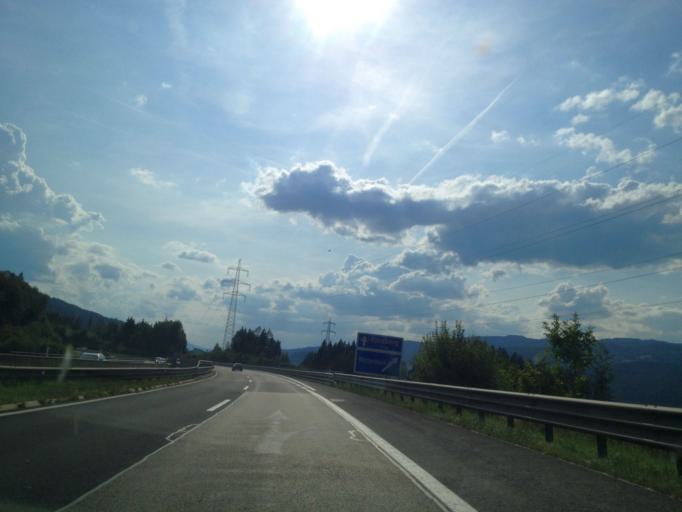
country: AT
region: Styria
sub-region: Politischer Bezirk Bruck-Muerzzuschlag
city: Mitterdorf im Muerztal
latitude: 47.5333
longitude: 15.5266
